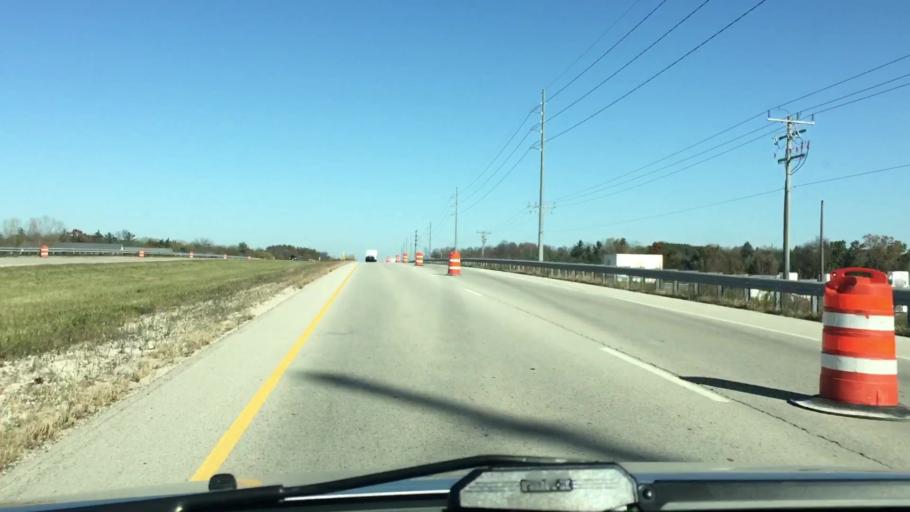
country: US
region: Wisconsin
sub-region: Waukesha County
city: Pewaukee
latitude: 43.0718
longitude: -88.2056
